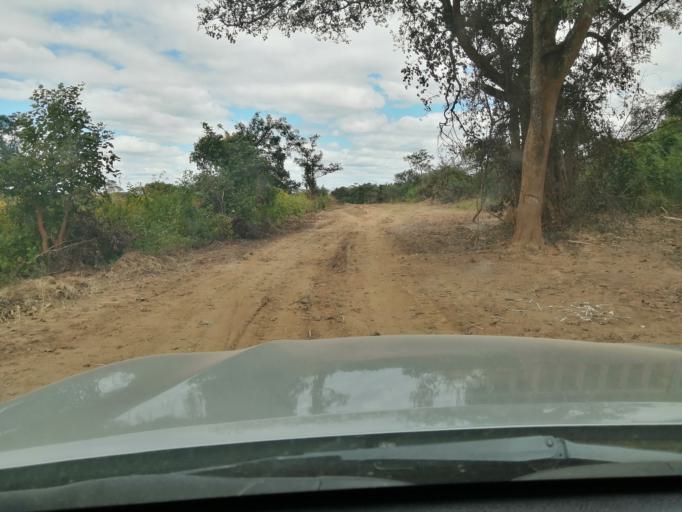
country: ZM
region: Central
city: Mumbwa
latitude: -14.5974
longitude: 27.1916
